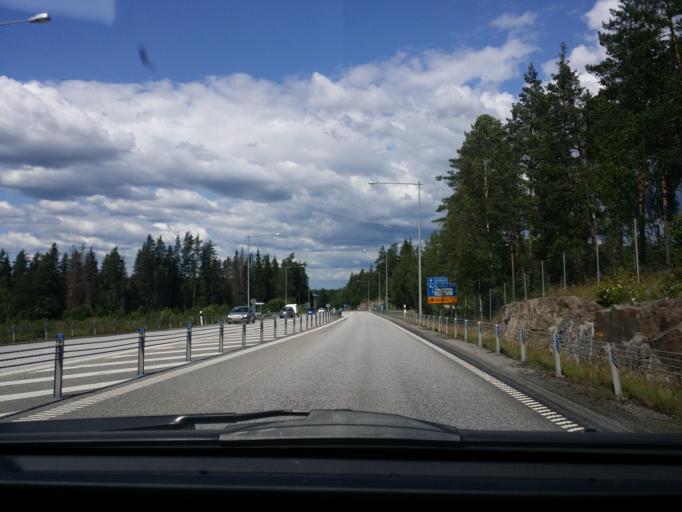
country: SE
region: OErebro
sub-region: Orebro Kommun
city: Hovsta
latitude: 59.3829
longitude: 15.2170
